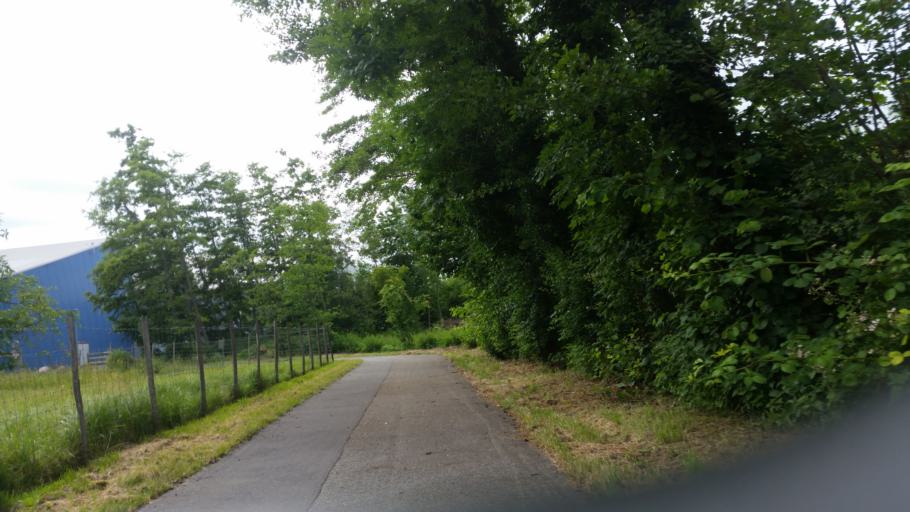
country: CH
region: Vaud
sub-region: Jura-Nord vaudois District
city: Yverdon-les-Bains
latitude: 46.7800
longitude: 6.6557
